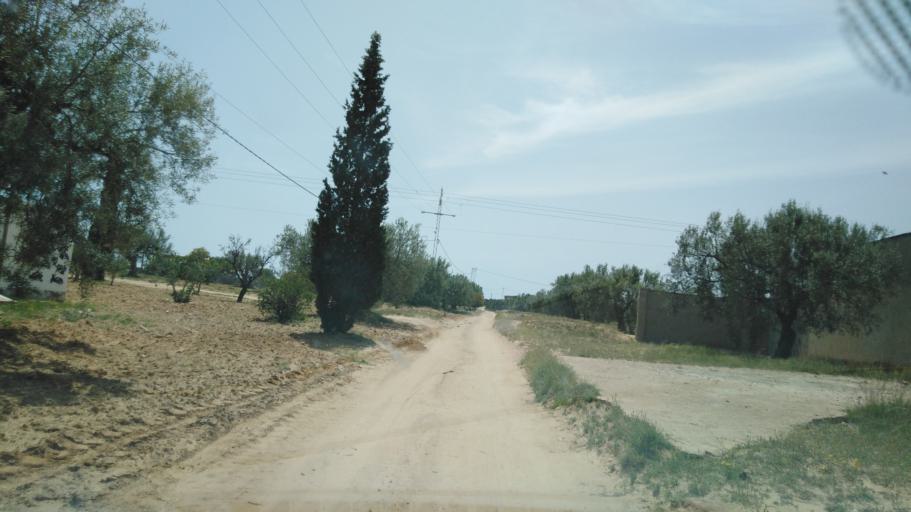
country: TN
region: Safaqis
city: Sfax
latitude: 34.7308
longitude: 10.5558
